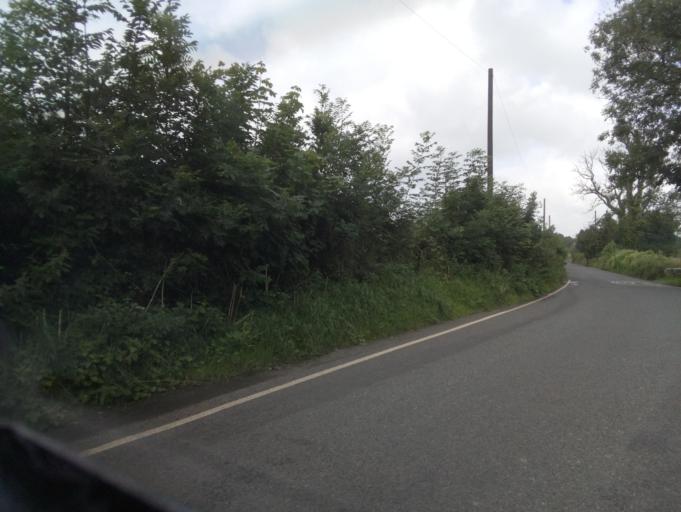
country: GB
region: England
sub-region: Somerset
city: Chilcompton
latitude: 51.2224
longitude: -2.5175
